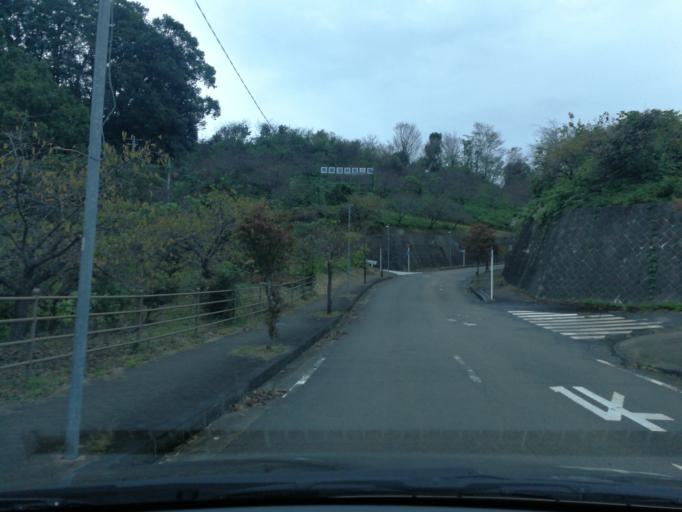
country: JP
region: Yamanashi
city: Uenohara
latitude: 35.6001
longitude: 139.2104
